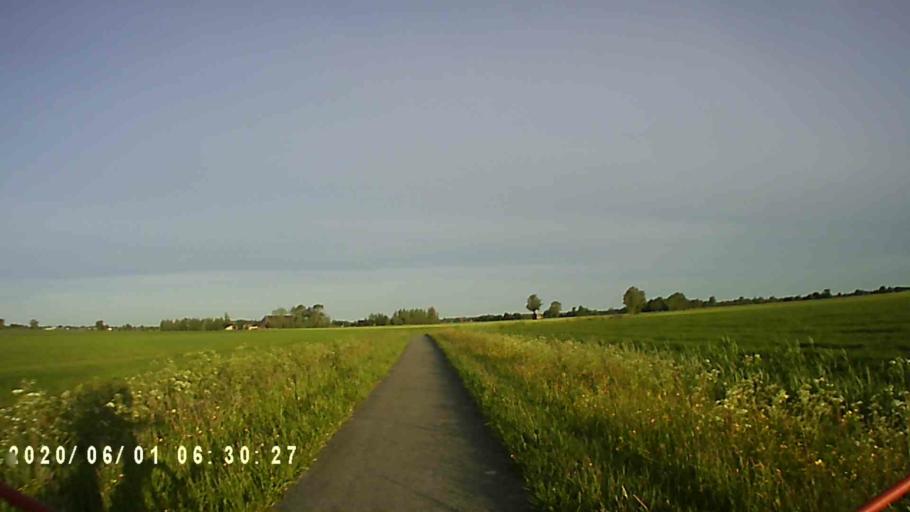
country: NL
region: Friesland
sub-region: Gemeente Kollumerland en Nieuwkruisland
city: Kollum
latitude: 53.2711
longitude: 6.1849
